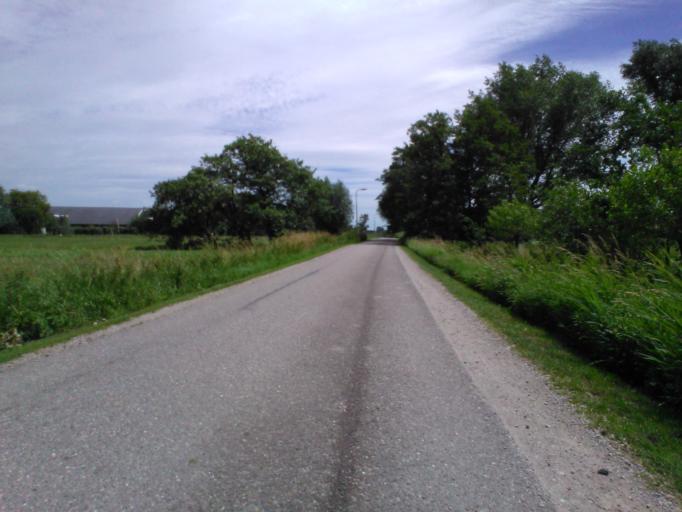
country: NL
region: South Holland
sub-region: Gemeente Sliedrecht
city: Sliedrecht
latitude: 51.8460
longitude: 4.7837
